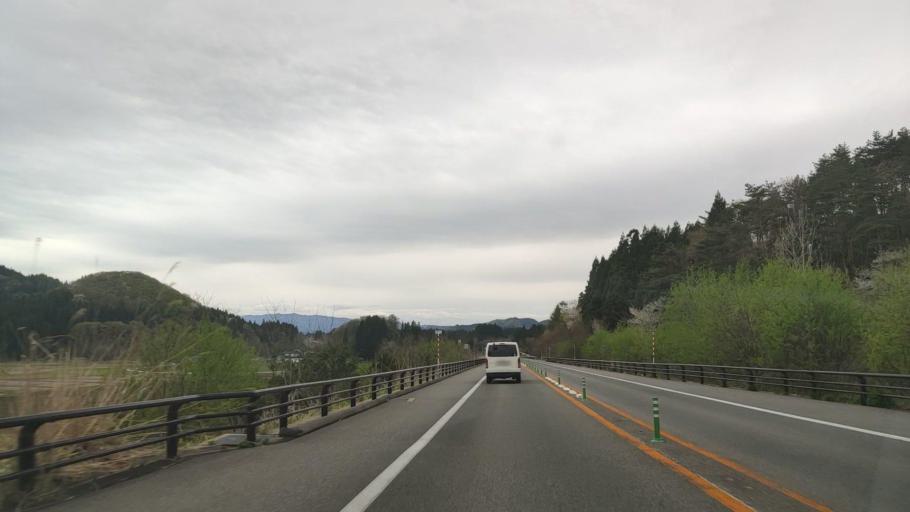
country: JP
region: Akita
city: Odate
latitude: 40.3177
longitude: 140.5867
